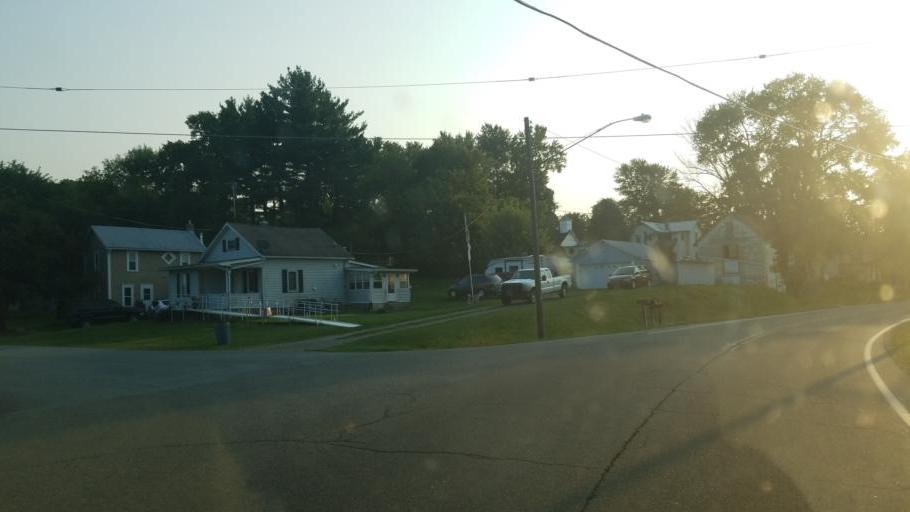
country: US
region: Ohio
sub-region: Wayne County
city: Shreve
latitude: 40.6678
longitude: -82.0916
